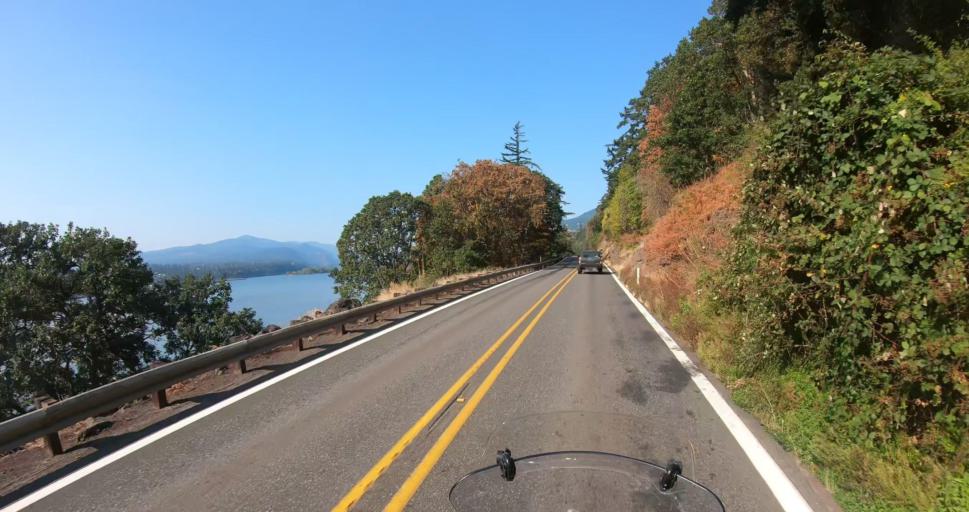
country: US
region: Washington
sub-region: Klickitat County
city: White Salmon
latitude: 45.7260
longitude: -121.5013
